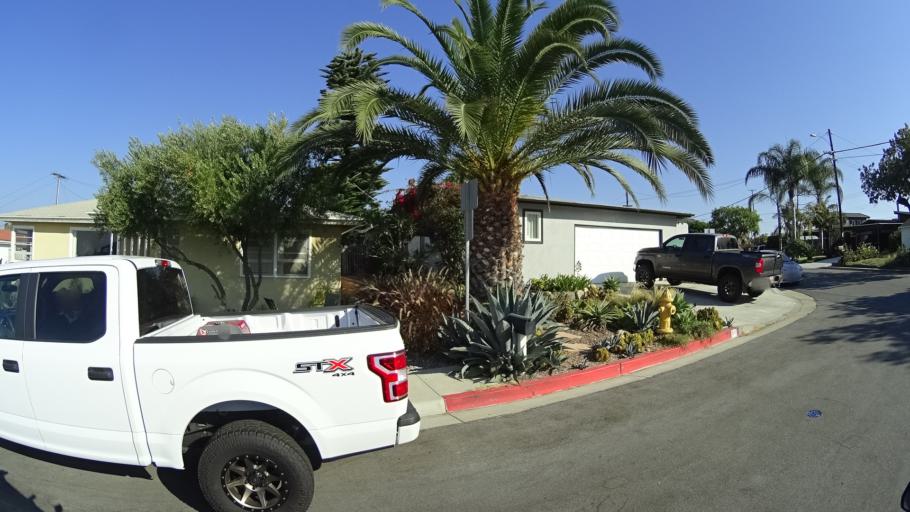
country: US
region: California
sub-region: Orange County
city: San Clemente
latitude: 33.4008
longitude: -117.5932
